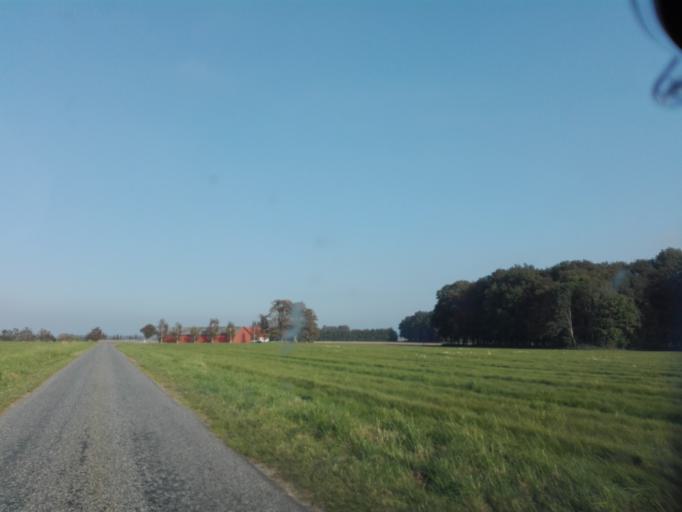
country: DK
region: Central Jutland
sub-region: Odder Kommune
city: Odder
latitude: 55.8790
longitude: 10.1480
